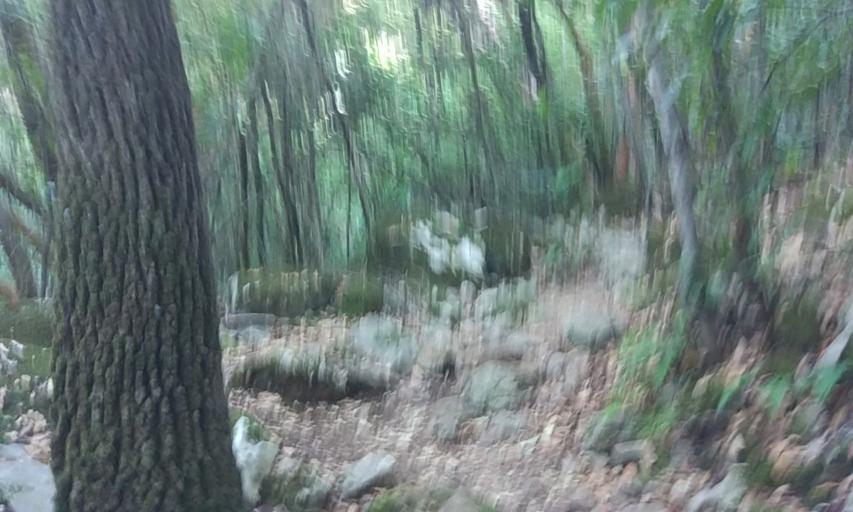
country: TR
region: Antalya
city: Tekirova
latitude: 36.3777
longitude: 30.4791
